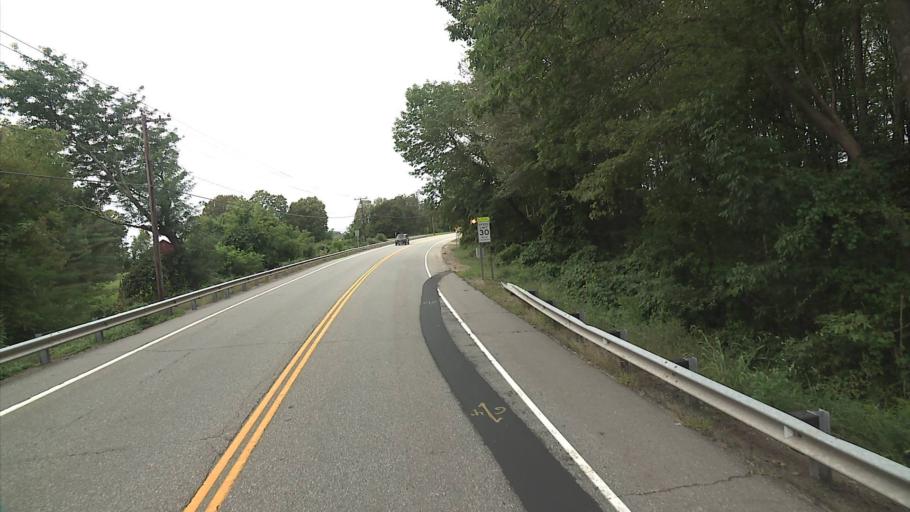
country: US
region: Connecticut
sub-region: Tolland County
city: Hebron
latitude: 41.6745
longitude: -72.4075
